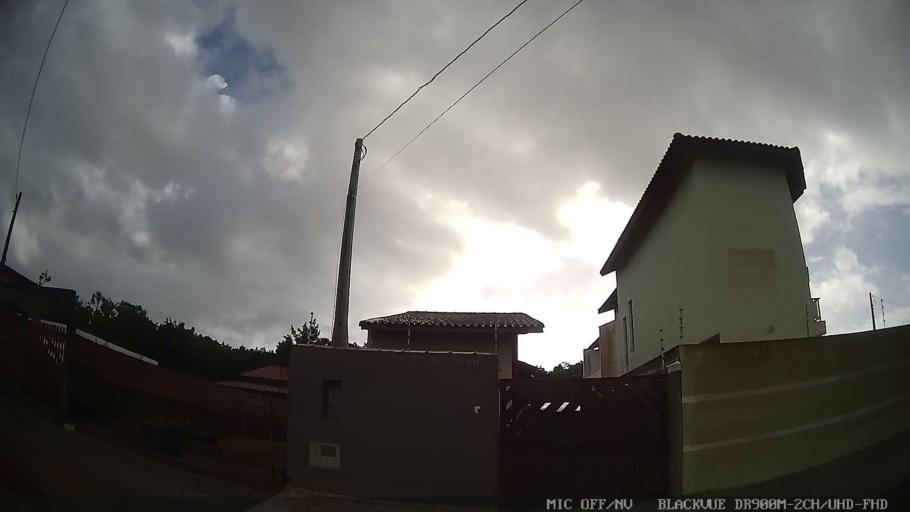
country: BR
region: Sao Paulo
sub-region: Itanhaem
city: Itanhaem
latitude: -24.1990
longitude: -46.8277
